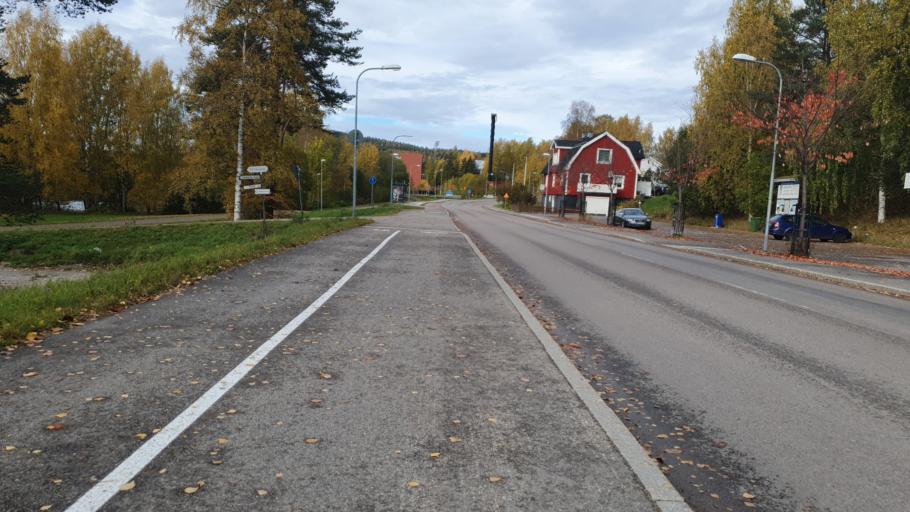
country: SE
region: Vaesternorrland
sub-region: Sundsvalls Kommun
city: Sundsvall
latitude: 62.4103
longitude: 17.2291
